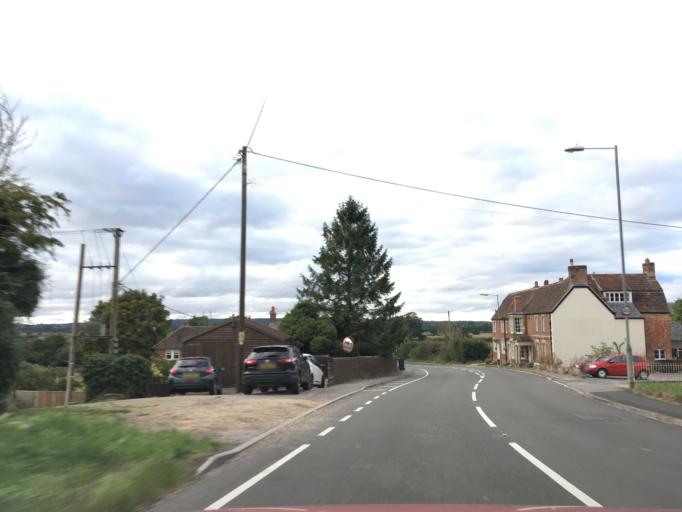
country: GB
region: England
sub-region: Wiltshire
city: Devizes
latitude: 51.3556
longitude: -2.0095
